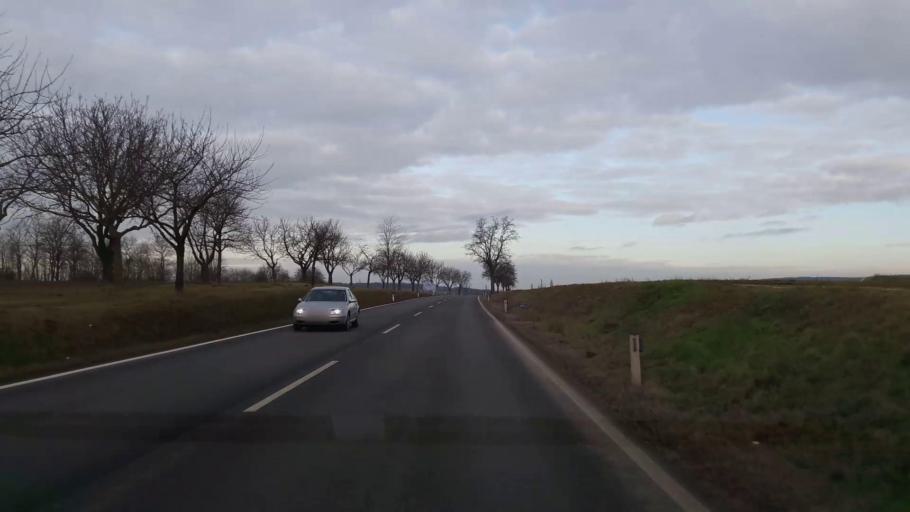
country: AT
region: Lower Austria
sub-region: Politischer Bezirk Mistelbach
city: Mistelbach
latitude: 48.5910
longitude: 16.5501
